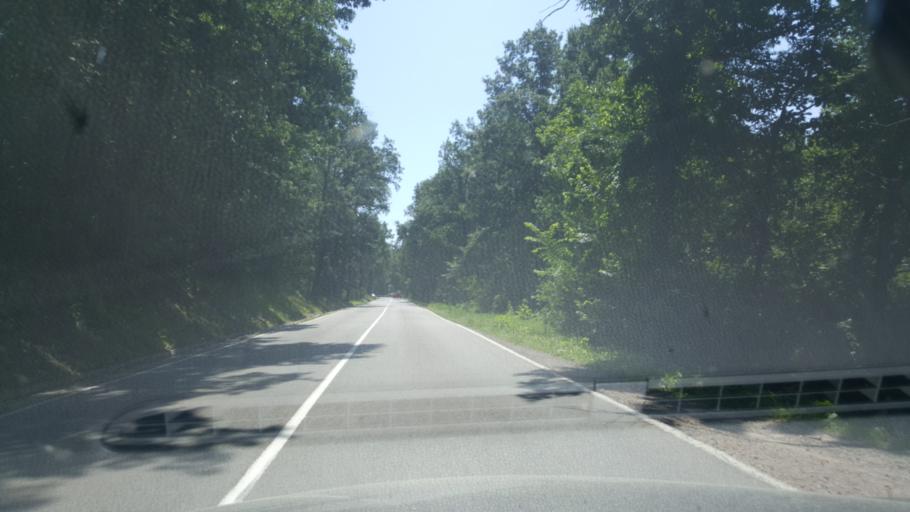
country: RS
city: Rusanj
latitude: 44.6830
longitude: 20.5147
